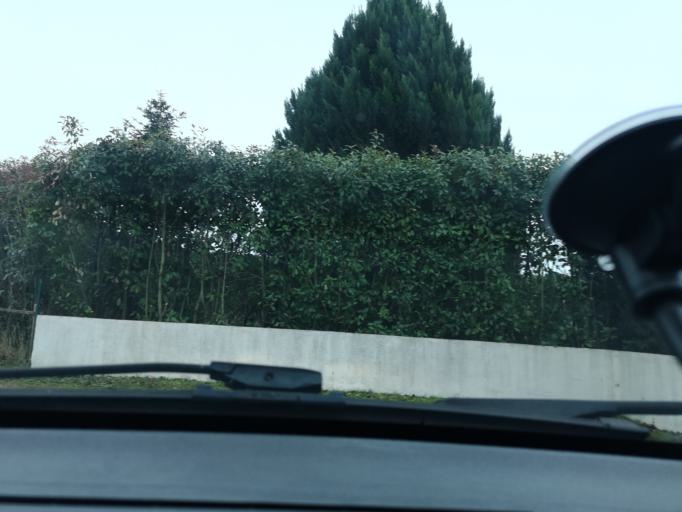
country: FR
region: Bourgogne
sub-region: Departement de Saone-et-Loire
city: Crissey
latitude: 46.8230
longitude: 4.8791
